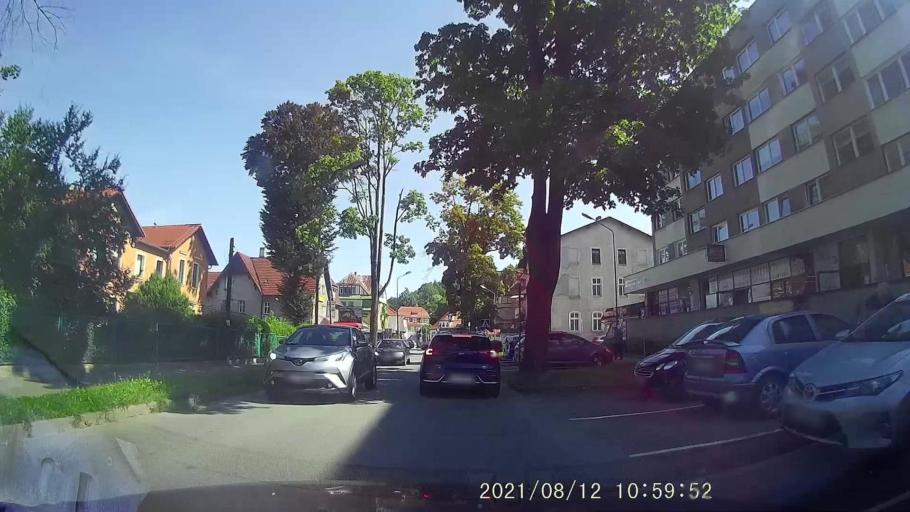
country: PL
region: Lower Silesian Voivodeship
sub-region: Powiat klodzki
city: Polanica-Zdroj
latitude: 50.4036
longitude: 16.5115
